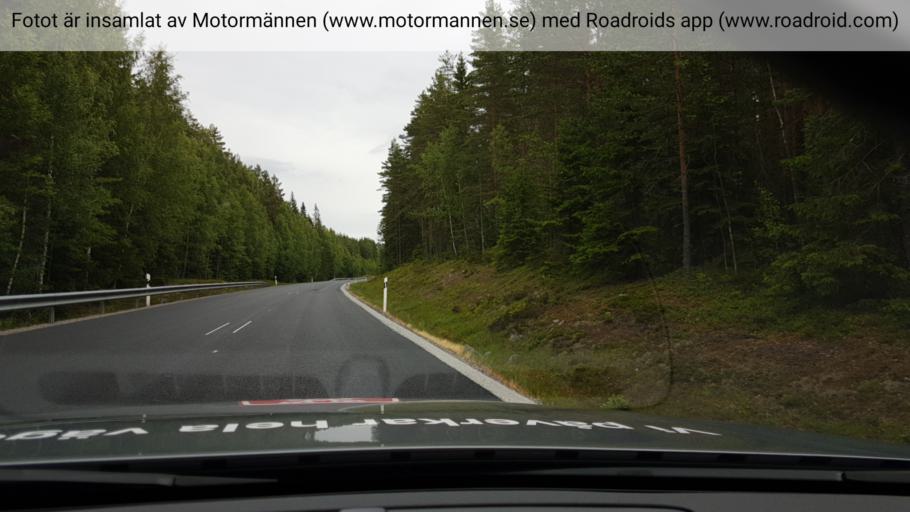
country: SE
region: Vaestmanland
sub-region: Skinnskattebergs Kommun
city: Skinnskatteberg
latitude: 59.8621
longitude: 15.5947
